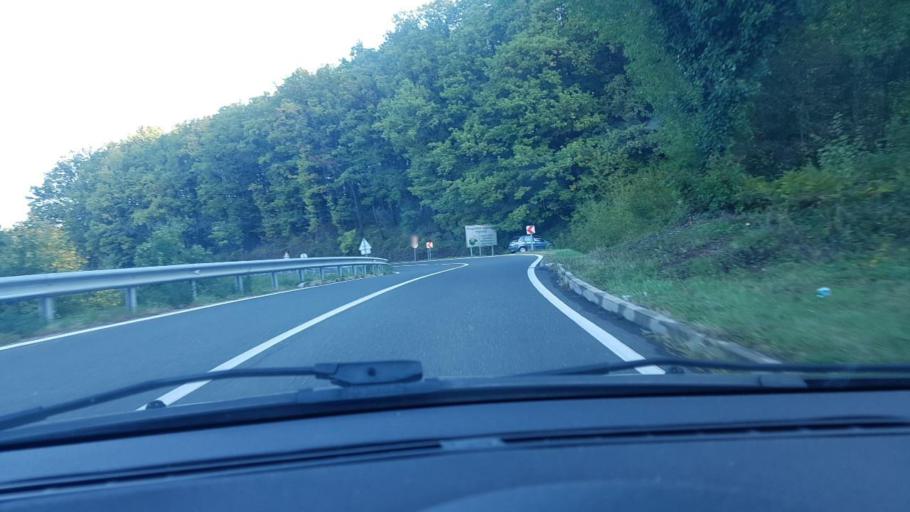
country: HR
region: Krapinsko-Zagorska
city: Marija Bistrica
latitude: 45.9530
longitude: 16.0964
